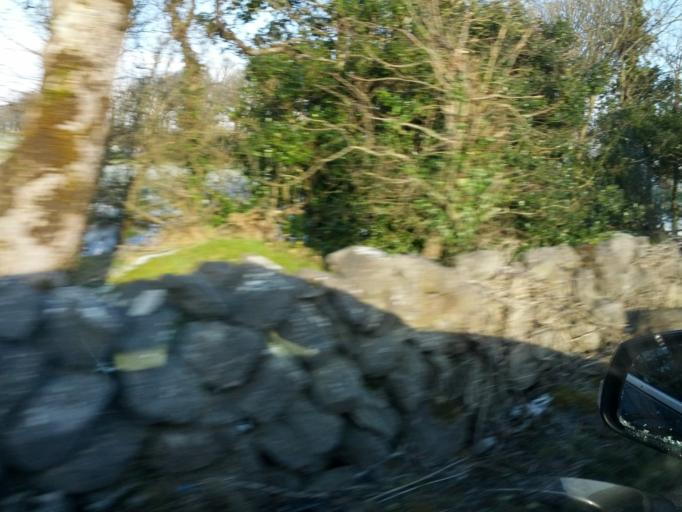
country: IE
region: Connaught
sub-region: County Galway
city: Gort
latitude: 53.1639
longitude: -8.7693
